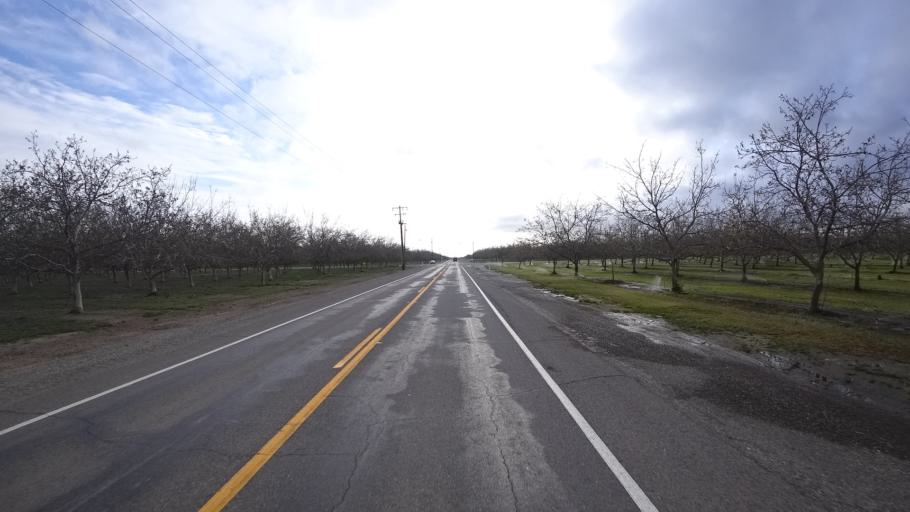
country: US
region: California
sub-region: Glenn County
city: Willows
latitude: 39.4643
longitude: -121.9696
